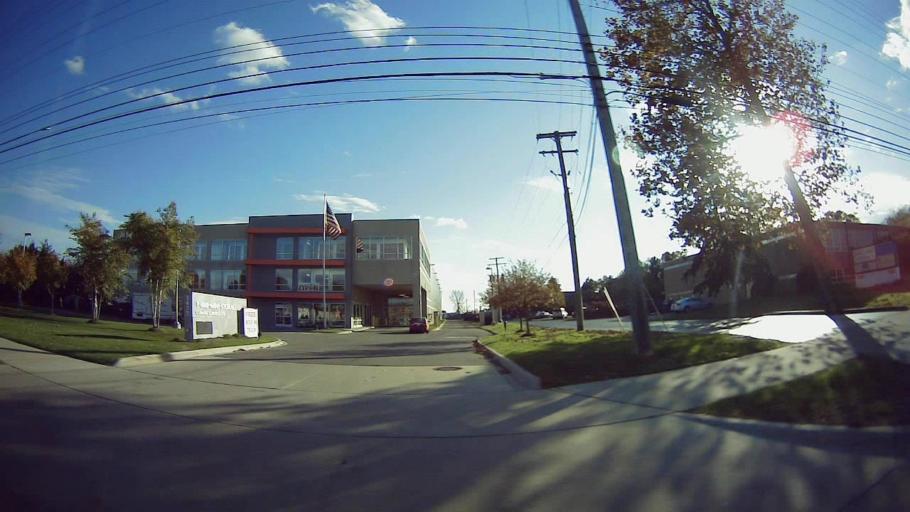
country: US
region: Michigan
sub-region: Oakland County
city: Birmingham
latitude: 42.5475
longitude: -83.1802
